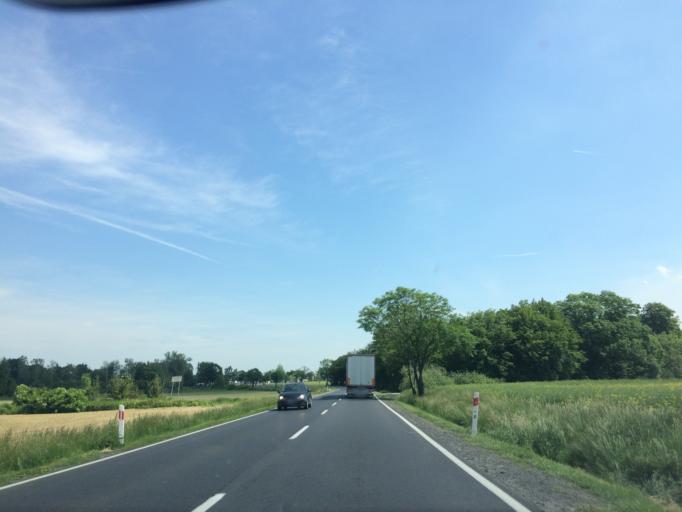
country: PL
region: Lower Silesian Voivodeship
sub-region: Powiat wroclawski
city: Sobotka
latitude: 50.9497
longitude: 16.7562
